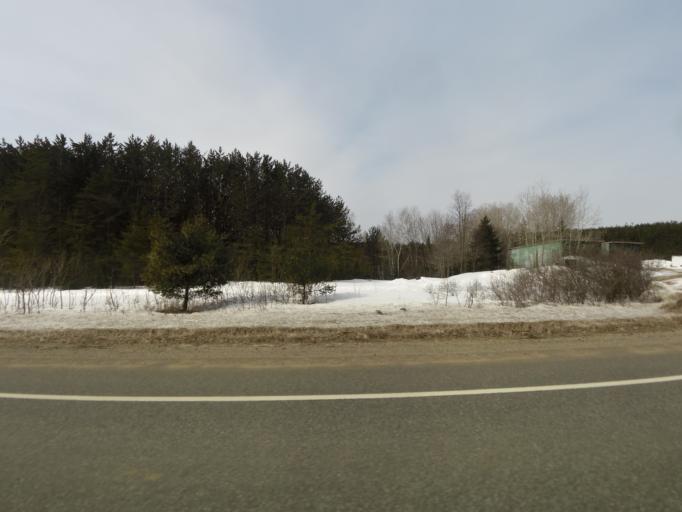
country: CA
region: Quebec
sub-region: Outaouais
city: Val-des-Monts
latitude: 45.9561
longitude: -75.5791
